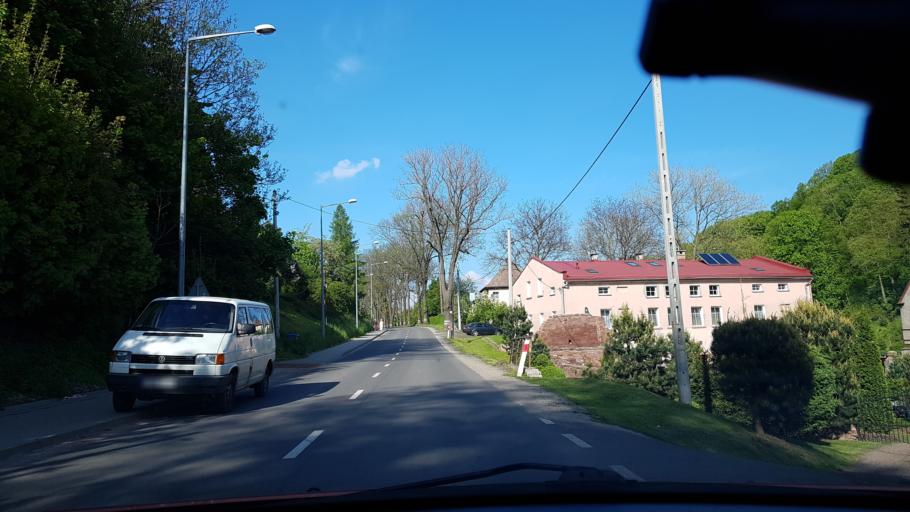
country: PL
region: Lower Silesian Voivodeship
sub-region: Powiat klodzki
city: Nowa Ruda
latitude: 50.5761
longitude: 16.4780
